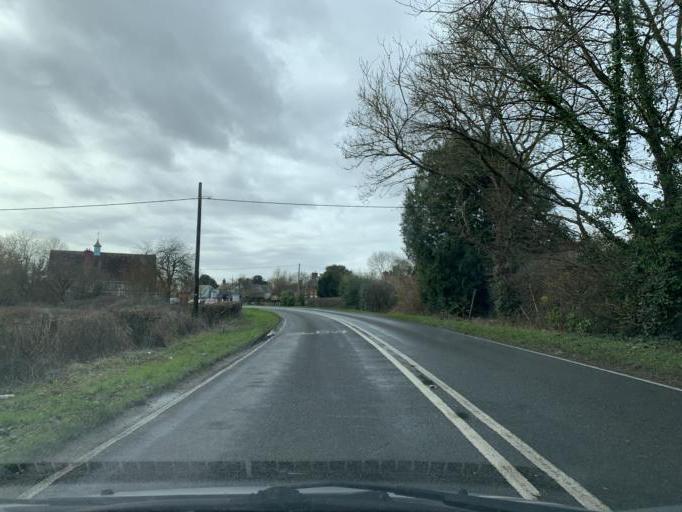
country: GB
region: England
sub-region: Hampshire
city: Fordingbridge
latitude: 50.9623
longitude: -1.7741
